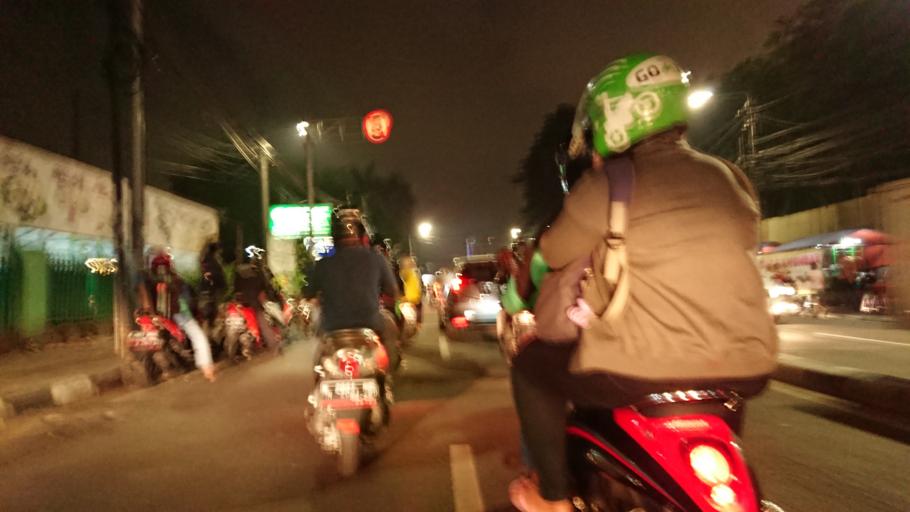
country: ID
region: Jakarta Raya
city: Jakarta
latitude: -6.2002
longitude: 106.8003
